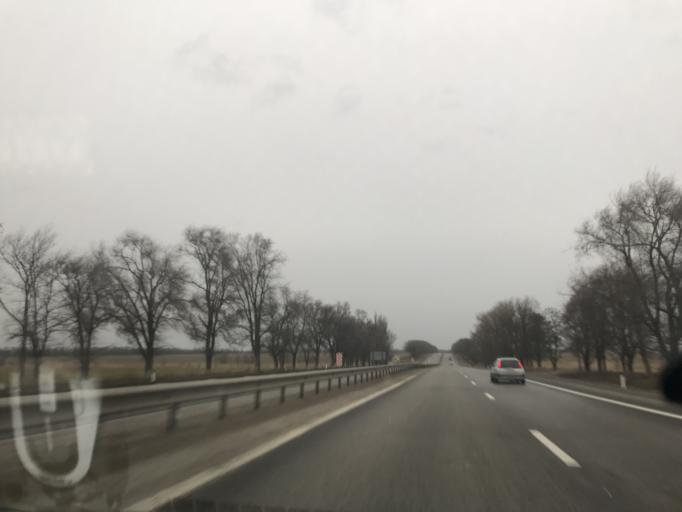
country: RU
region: Krasnodarskiy
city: Pavlovskaya
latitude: 46.1648
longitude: 39.8422
